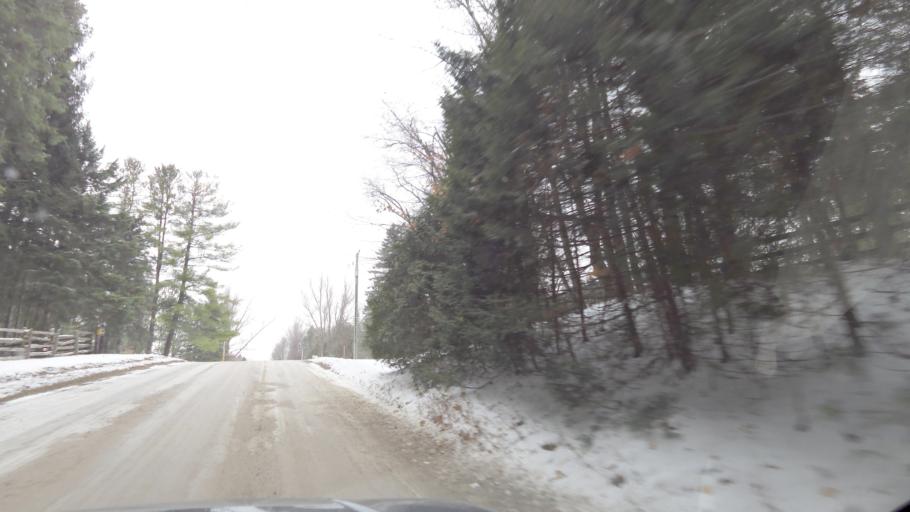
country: CA
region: Ontario
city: Vaughan
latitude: 43.9220
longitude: -79.6055
